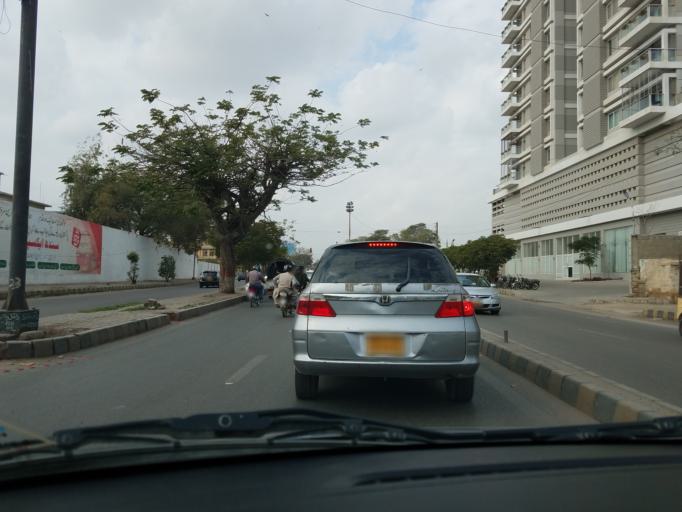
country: PK
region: Sindh
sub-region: Karachi District
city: Karachi
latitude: 24.8426
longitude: 67.0324
